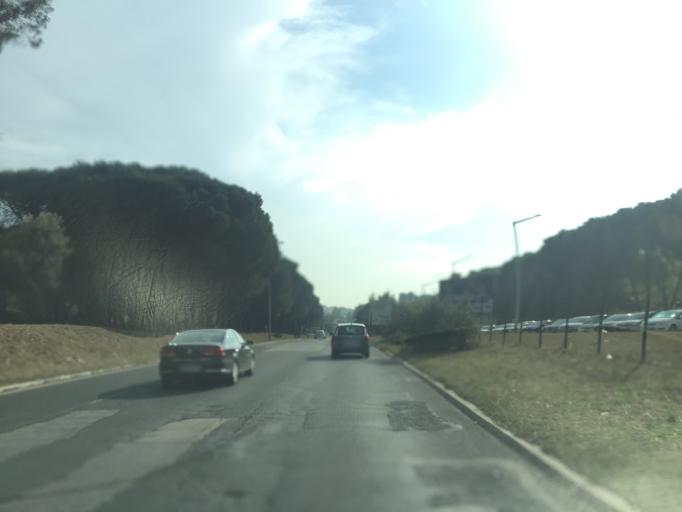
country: PT
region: Lisbon
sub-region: Loures
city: Moscavide
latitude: 38.7756
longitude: -9.1237
